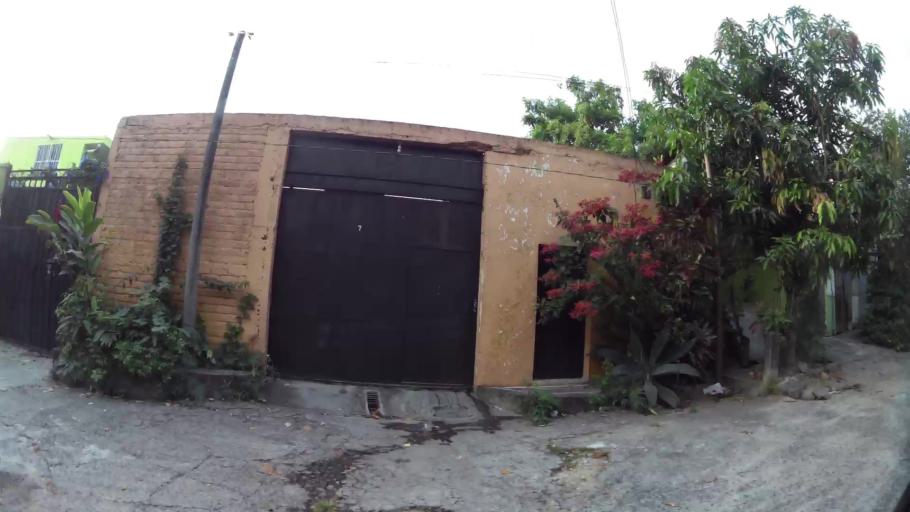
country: SV
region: San Salvador
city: San Salvador
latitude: 13.6924
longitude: -89.2042
